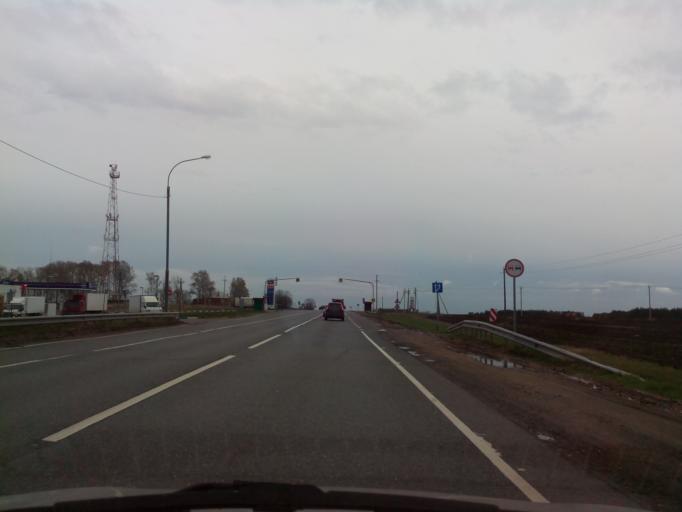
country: RU
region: Moskovskaya
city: Ozherel'ye
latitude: 54.7025
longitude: 38.3031
